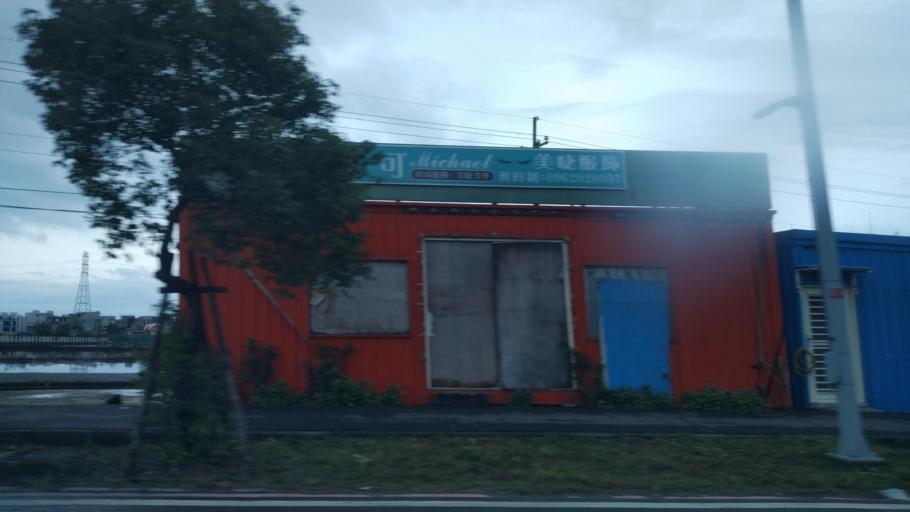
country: TW
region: Taiwan
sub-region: Yilan
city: Yilan
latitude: 24.6134
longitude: 121.8313
